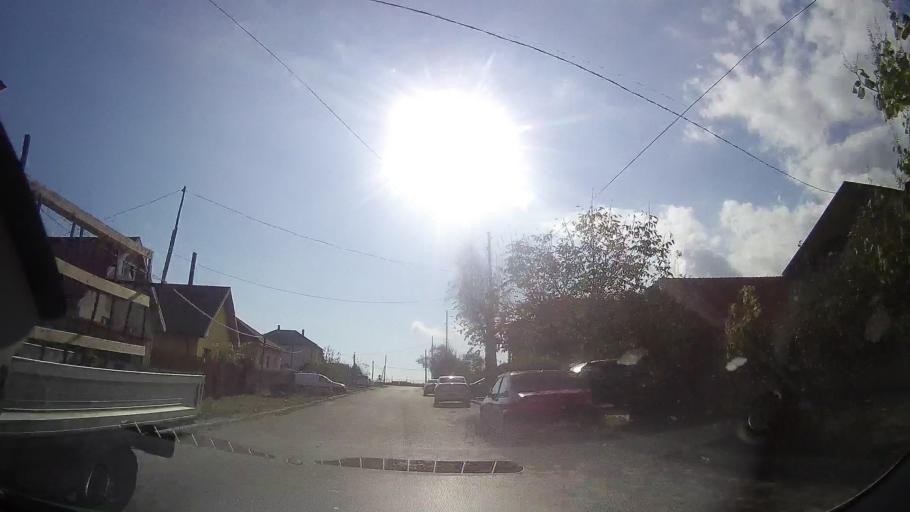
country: RO
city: Eforie Sud
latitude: 44.0154
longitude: 28.6474
